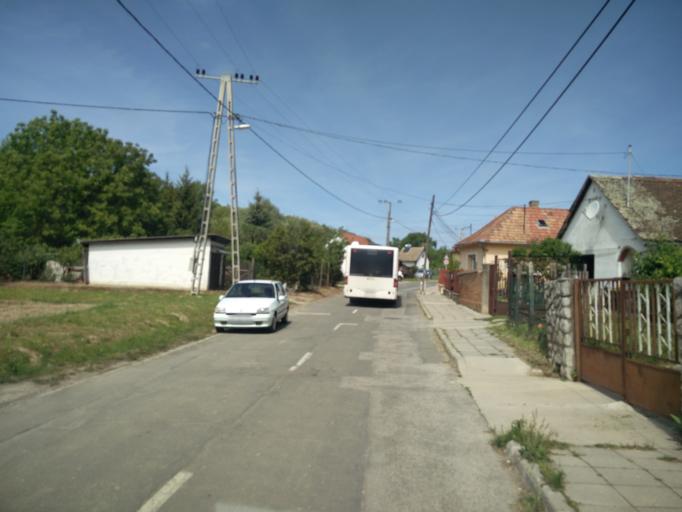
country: HU
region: Tolna
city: Szekszard
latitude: 46.3097
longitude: 18.6852
